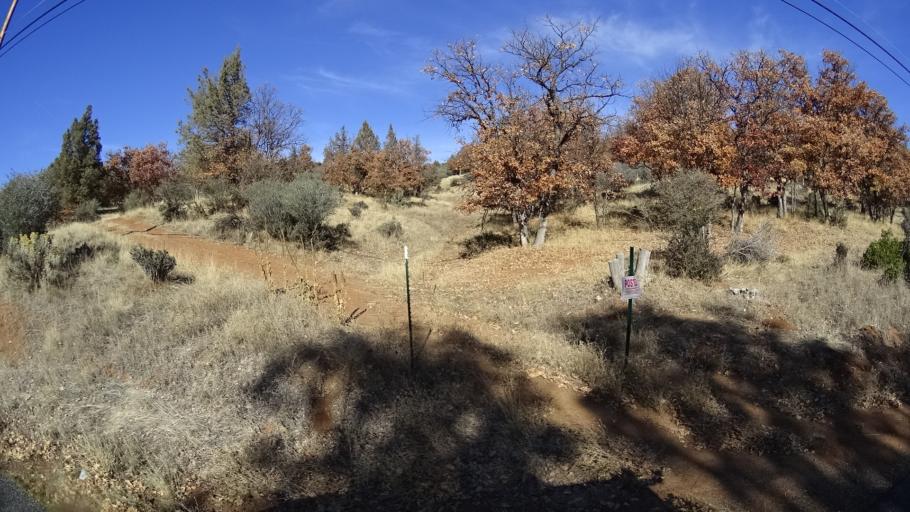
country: US
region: California
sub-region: Siskiyou County
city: Yreka
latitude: 41.7133
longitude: -122.6533
